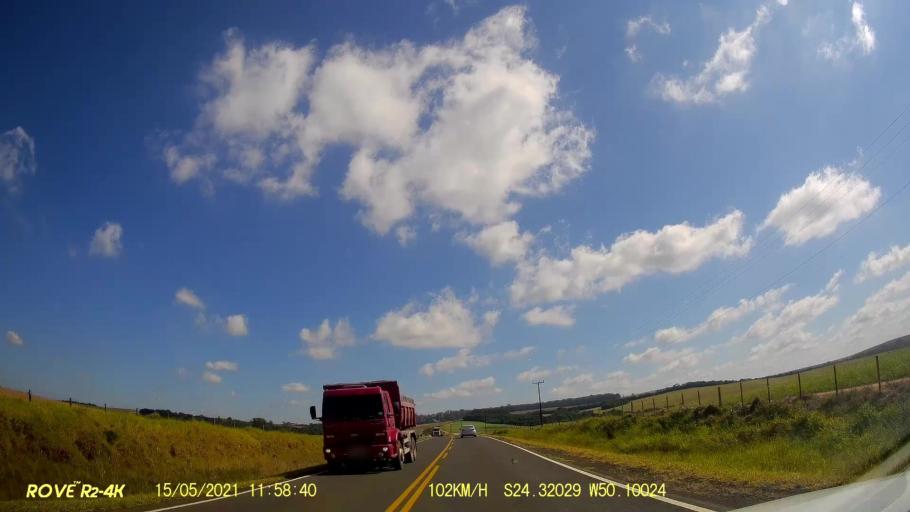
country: BR
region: Parana
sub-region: Pirai Do Sul
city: Pirai do Sul
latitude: -24.3211
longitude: -50.1004
